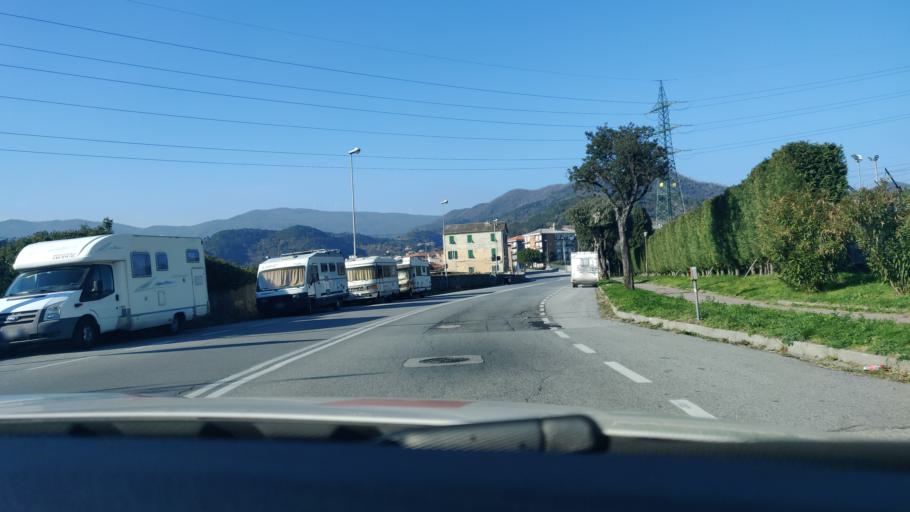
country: IT
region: Liguria
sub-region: Provincia di Savona
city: Quiliano
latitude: 44.2903
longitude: 8.4206
